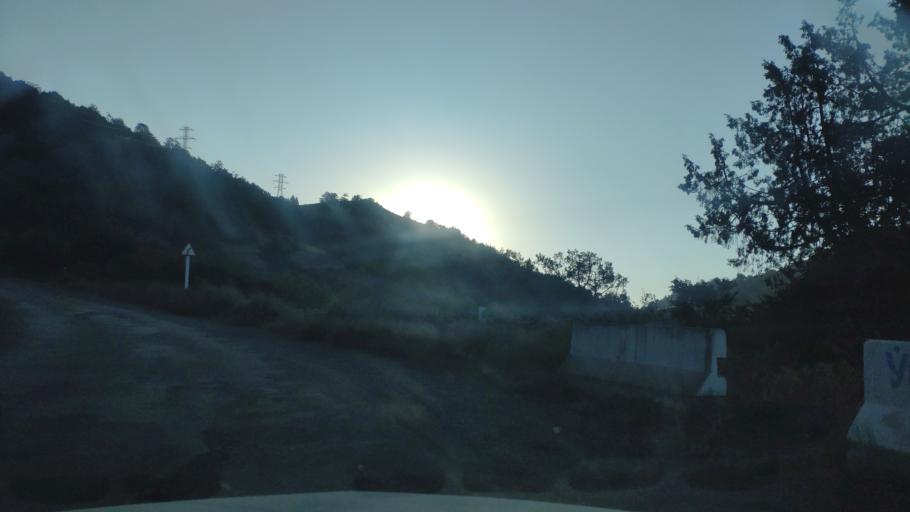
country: TJ
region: Viloyati Sughd
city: Ayni
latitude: 39.6394
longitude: 68.4759
